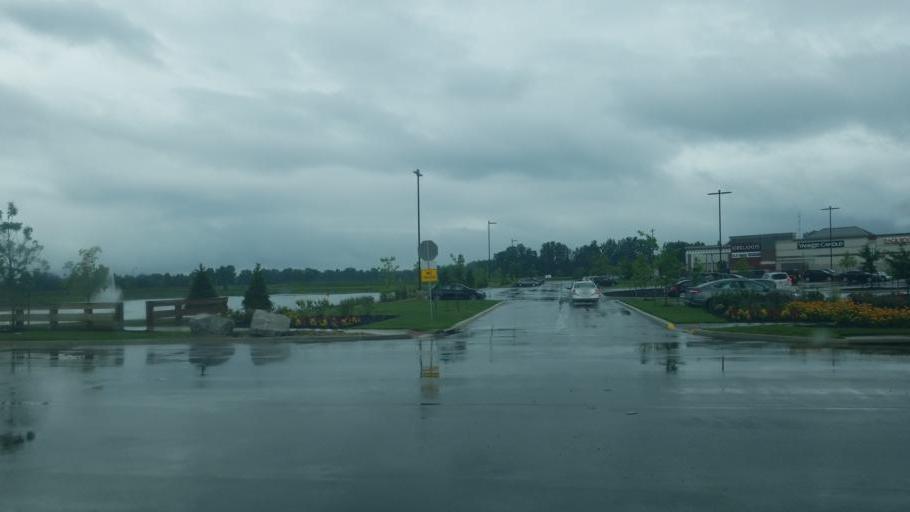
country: US
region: Ohio
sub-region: Delaware County
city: Sunbury
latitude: 40.2607
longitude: -82.9225
